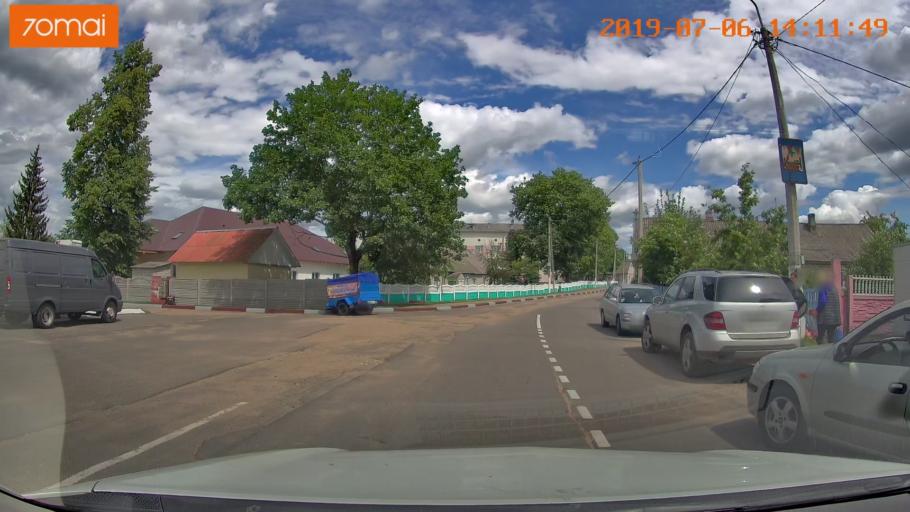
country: BY
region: Minsk
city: Ivyanyets
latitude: 53.8900
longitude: 26.7409
